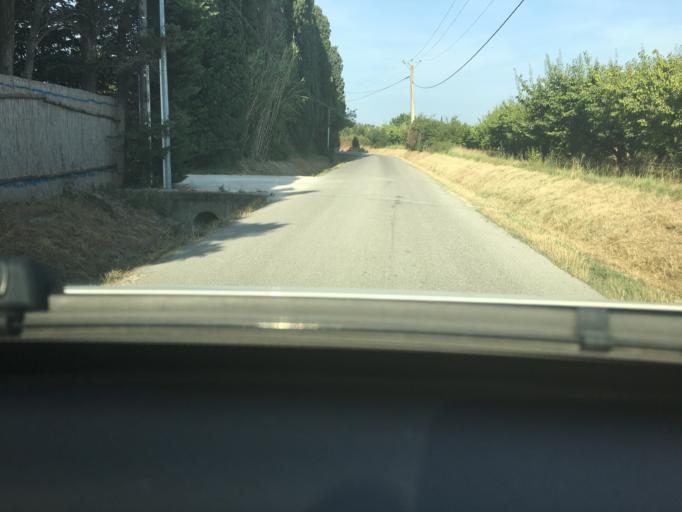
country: FR
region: Provence-Alpes-Cote d'Azur
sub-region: Departement des Bouches-du-Rhone
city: Maillane
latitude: 43.8316
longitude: 4.7954
